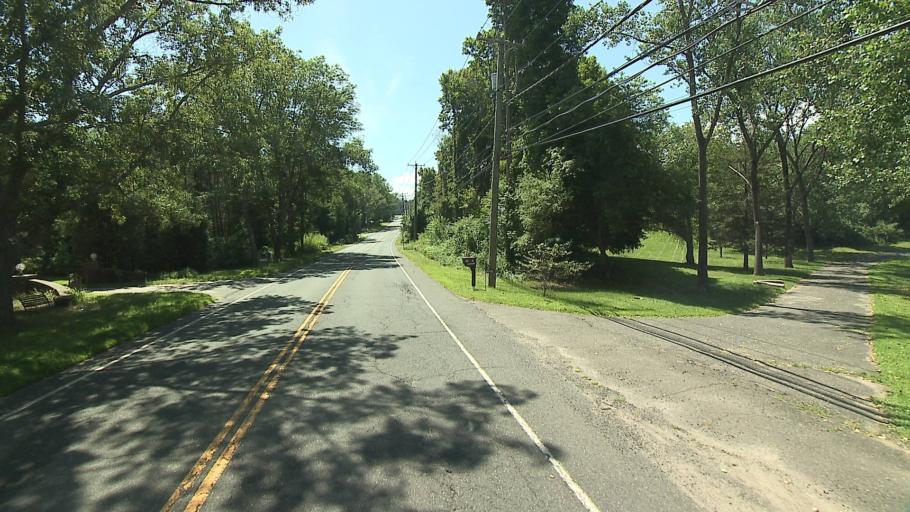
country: US
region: Connecticut
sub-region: Fairfield County
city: Trumbull
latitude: 41.3487
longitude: -73.1982
